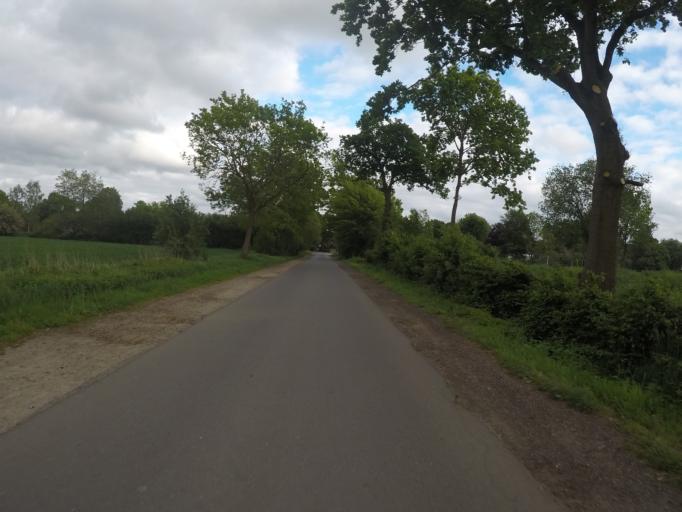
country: DE
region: Schleswig-Holstein
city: Hasloh
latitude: 53.7003
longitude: 9.9224
